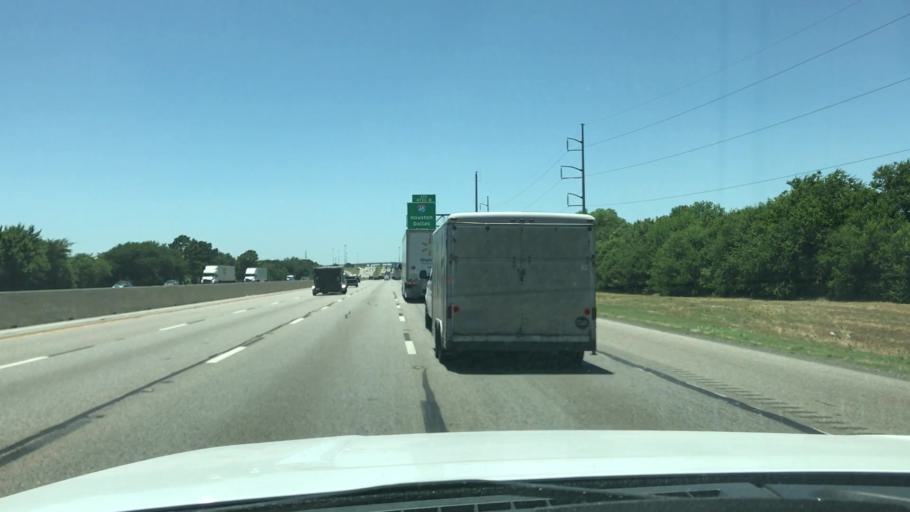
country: US
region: Texas
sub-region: Dallas County
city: Hutchins
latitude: 32.6720
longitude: -96.7067
